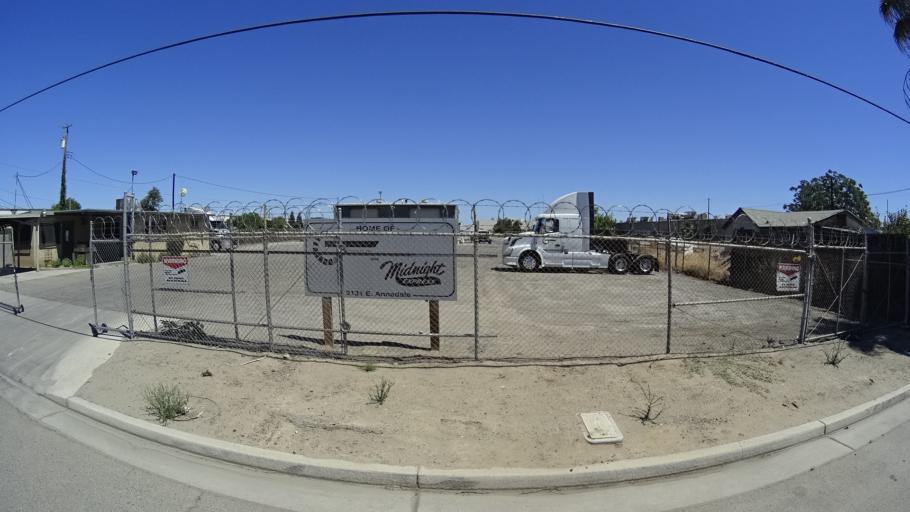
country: US
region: California
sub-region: Fresno County
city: Easton
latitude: 36.6996
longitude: -119.7852
